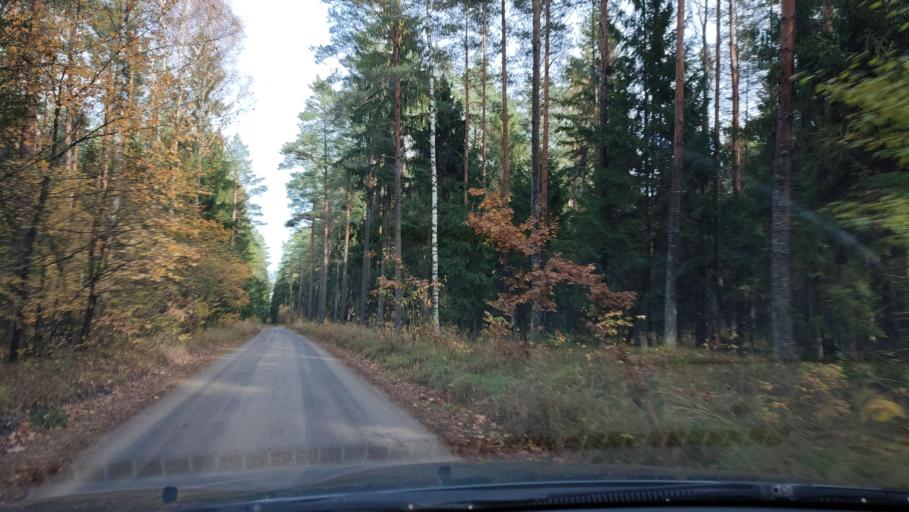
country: PL
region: Warmian-Masurian Voivodeship
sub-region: Powiat szczycienski
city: Szczytno
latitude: 53.5240
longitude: 20.8958
